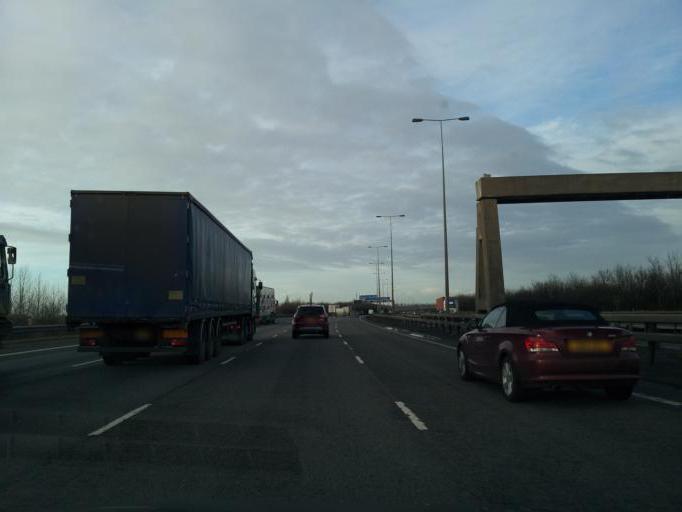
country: GB
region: England
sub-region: Cambridgeshire
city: Stilton
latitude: 52.4797
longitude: -0.2870
